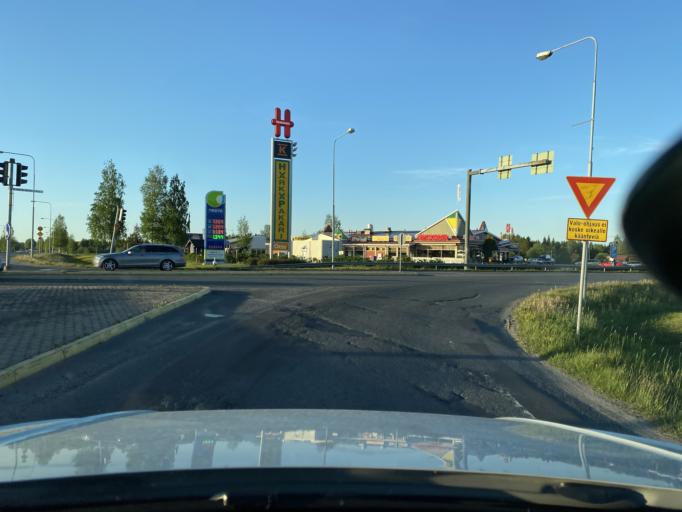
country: FI
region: Satakunta
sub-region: Pori
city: Huittinen
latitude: 61.1745
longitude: 22.6797
